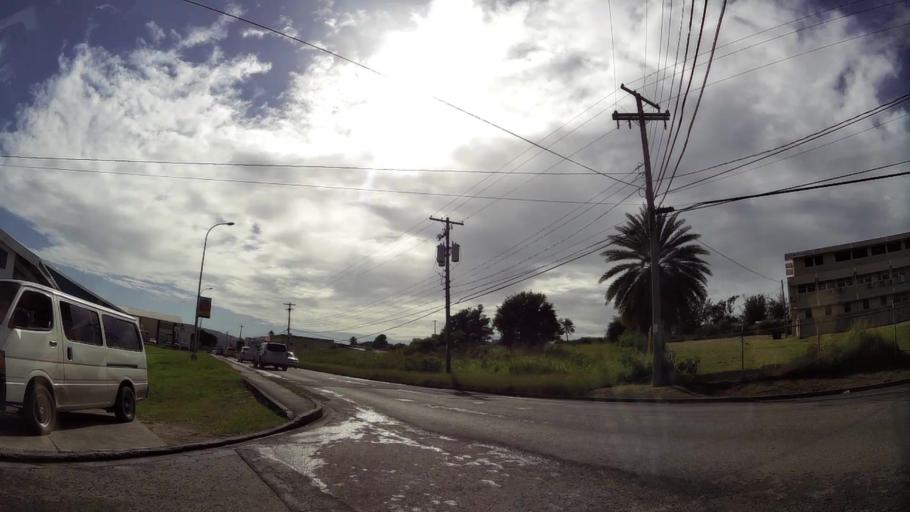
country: AG
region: Saint John
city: Saint John's
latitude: 17.1148
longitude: -61.8287
